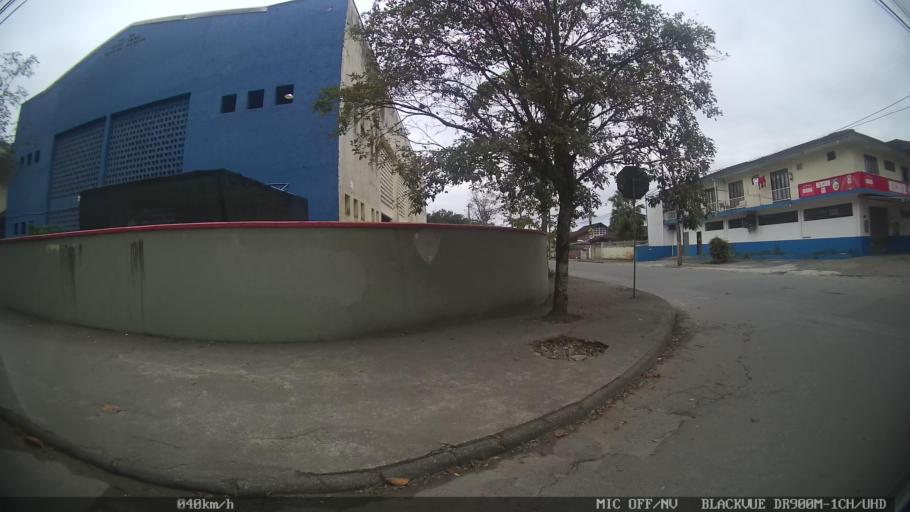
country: BR
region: Santa Catarina
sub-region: Joinville
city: Joinville
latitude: -26.2644
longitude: -48.8864
